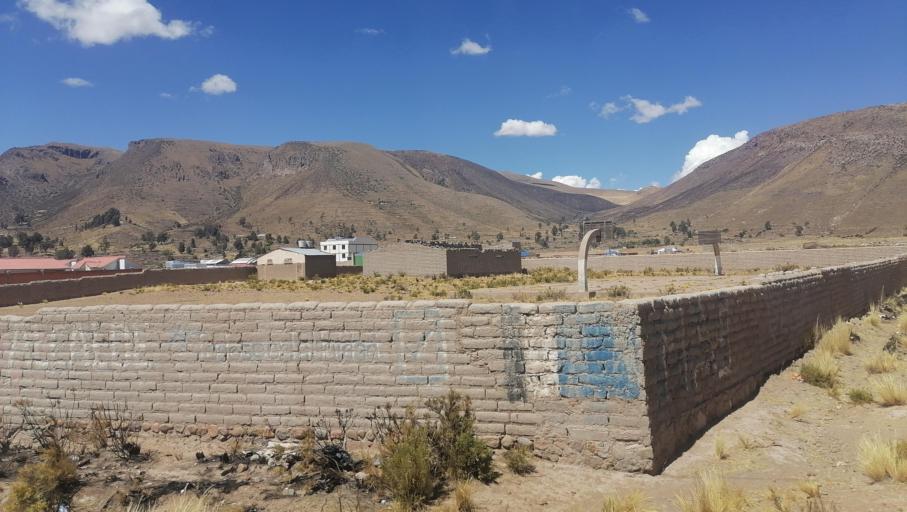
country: BO
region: Oruro
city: Challapata
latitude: -19.0215
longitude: -66.7774
